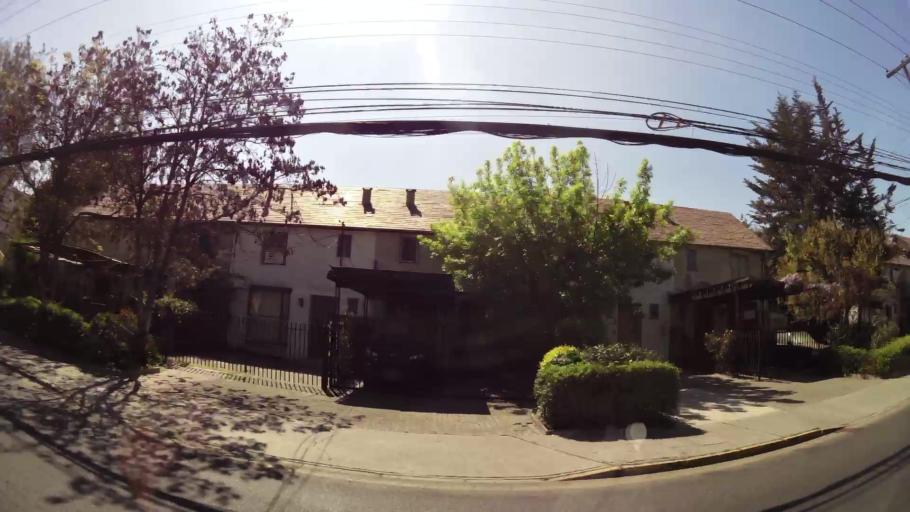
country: CL
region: Santiago Metropolitan
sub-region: Provincia de Santiago
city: Villa Presidente Frei, Nunoa, Santiago, Chile
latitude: -33.4081
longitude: -70.5551
